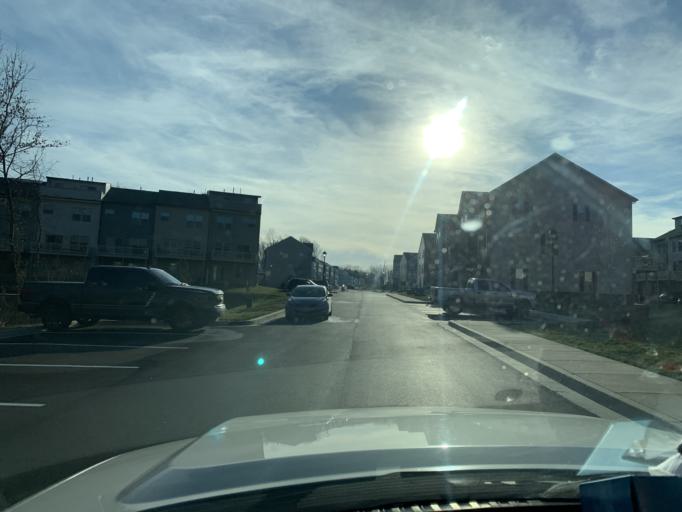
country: US
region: Maryland
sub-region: Anne Arundel County
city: Fort Meade
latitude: 39.1312
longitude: -76.7488
